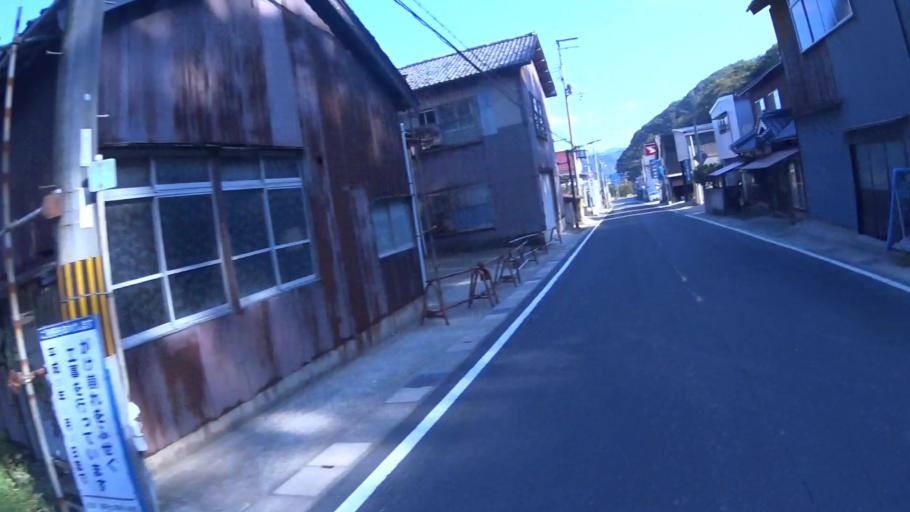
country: JP
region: Kyoto
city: Miyazu
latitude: 35.7328
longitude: 135.0942
